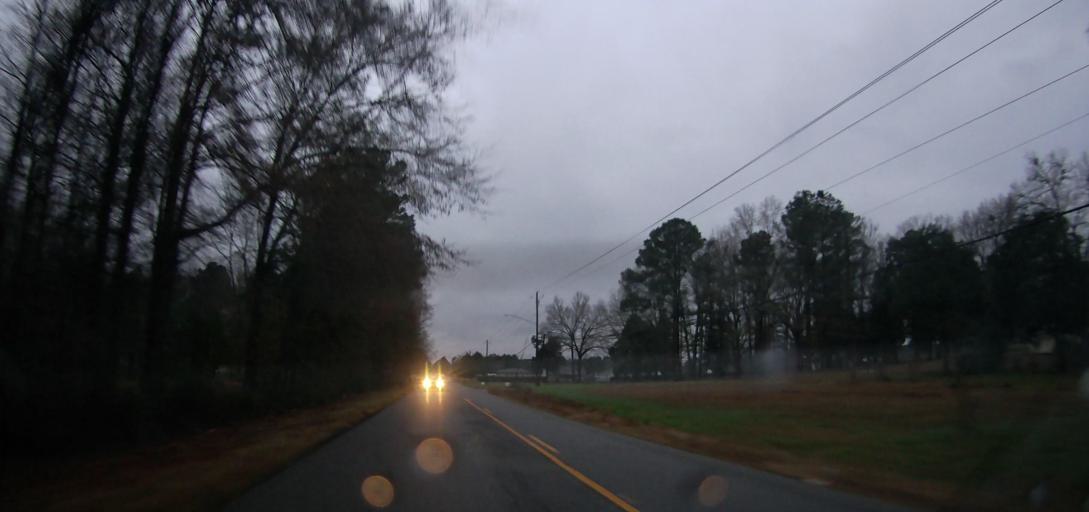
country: US
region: Alabama
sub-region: Tuscaloosa County
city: Vance
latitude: 33.1480
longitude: -87.2298
